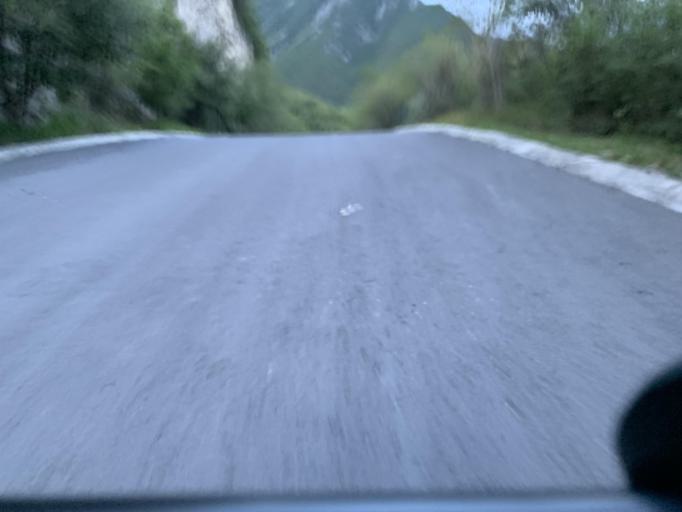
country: MX
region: Nuevo Leon
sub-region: Juarez
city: Bosques de San Pedro
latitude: 25.5204
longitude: -100.1860
